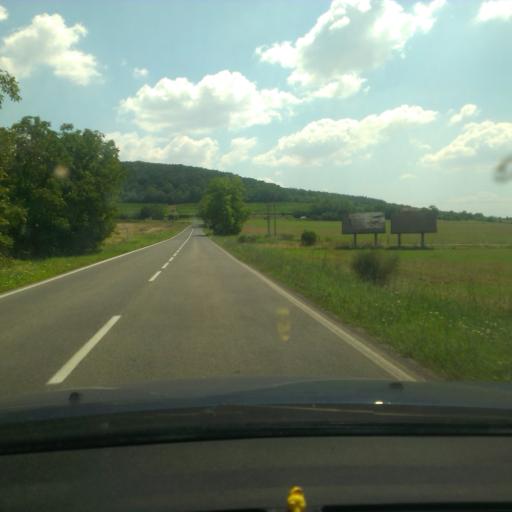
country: SK
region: Trnavsky
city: Hlohovec
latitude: 48.4639
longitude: 17.8145
